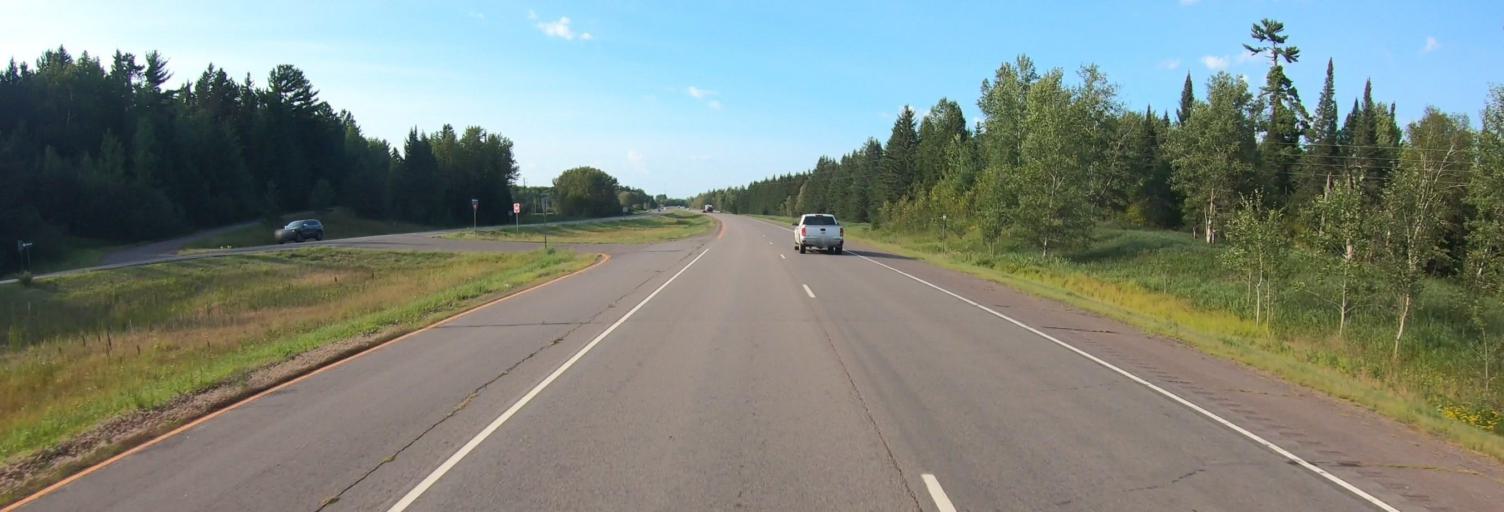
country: US
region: Minnesota
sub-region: Saint Louis County
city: Eveleth
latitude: 47.1289
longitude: -92.4722
